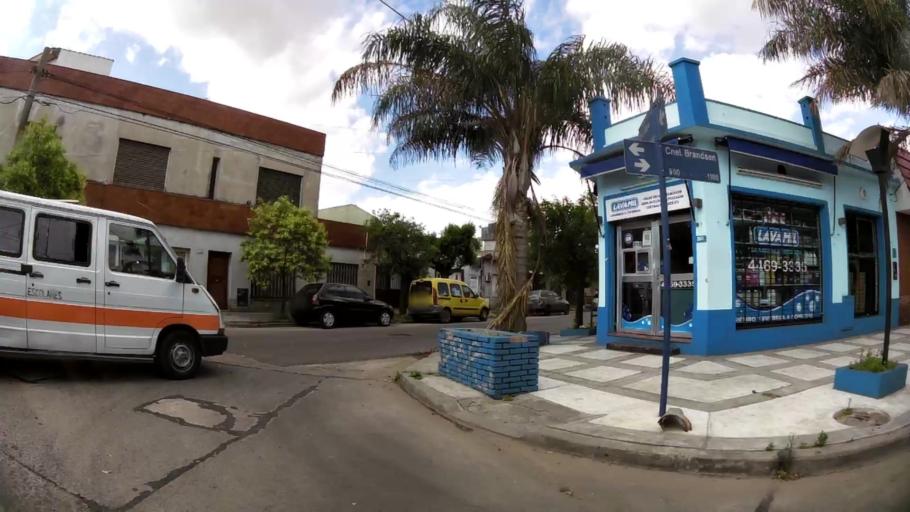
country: AR
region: Buenos Aires
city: San Justo
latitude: -34.6563
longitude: -58.5684
